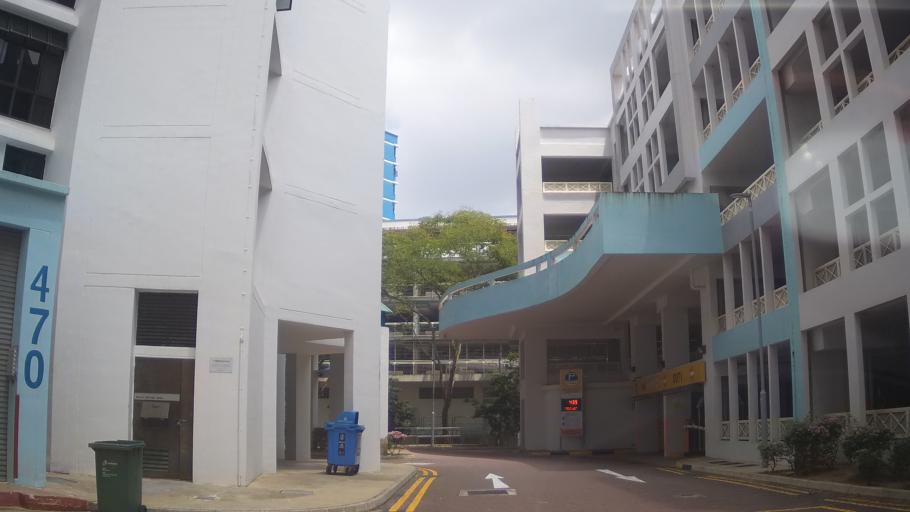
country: MY
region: Johor
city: Johor Bahru
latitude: 1.3883
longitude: 103.7733
